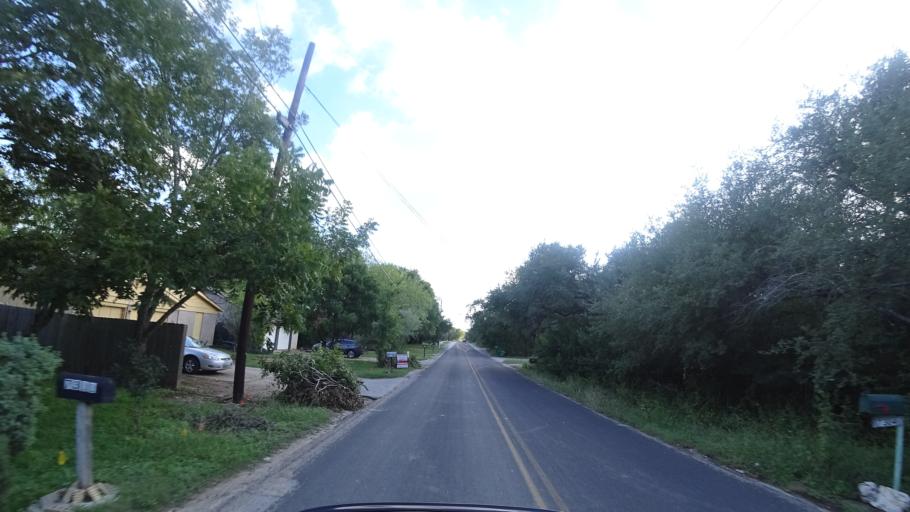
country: US
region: Texas
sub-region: Travis County
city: Onion Creek
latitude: 30.1912
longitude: -97.7942
